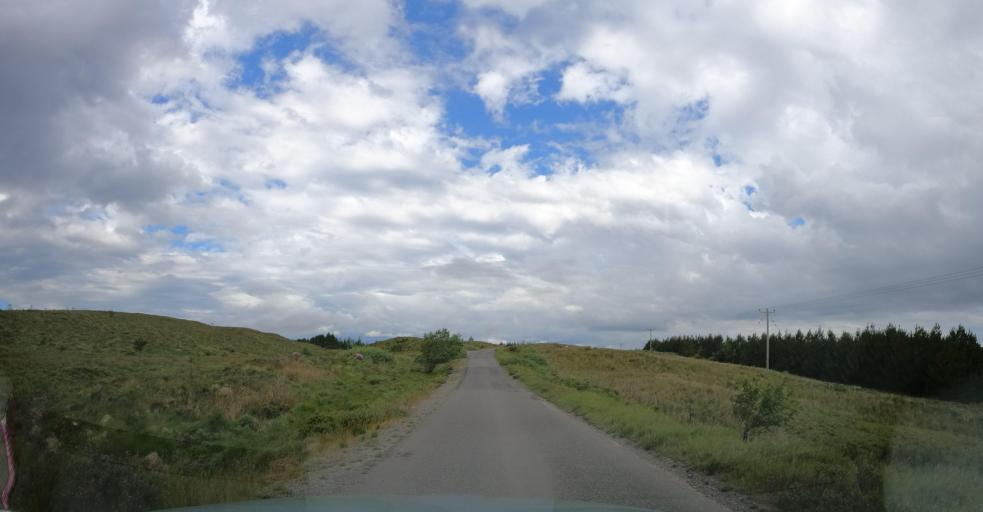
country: GB
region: Scotland
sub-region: Eilean Siar
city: Stornoway
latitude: 58.2015
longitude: -6.4085
